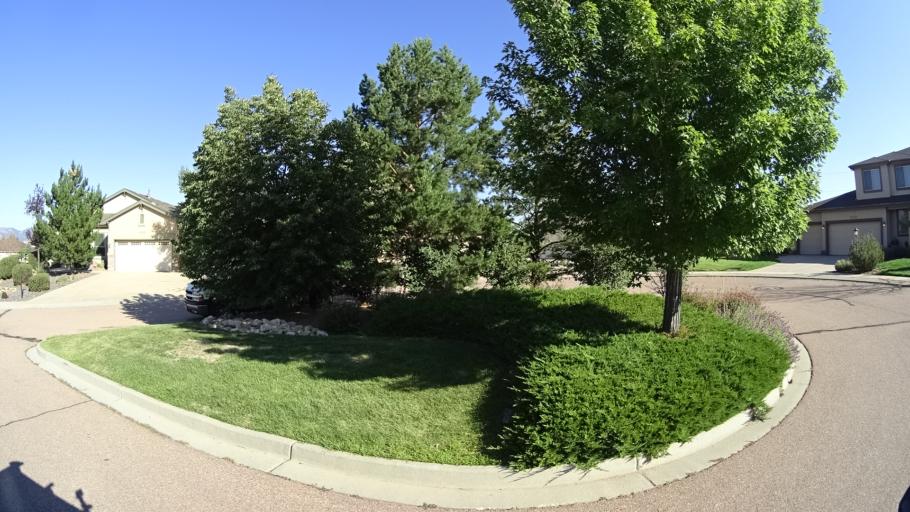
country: US
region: Colorado
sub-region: El Paso County
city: Black Forest
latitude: 38.9781
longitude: -104.7585
